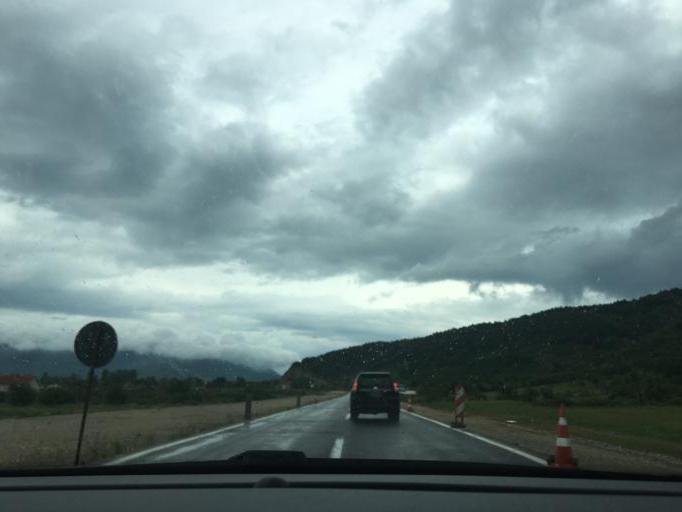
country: MK
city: Misleshevo
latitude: 41.1962
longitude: 20.7526
